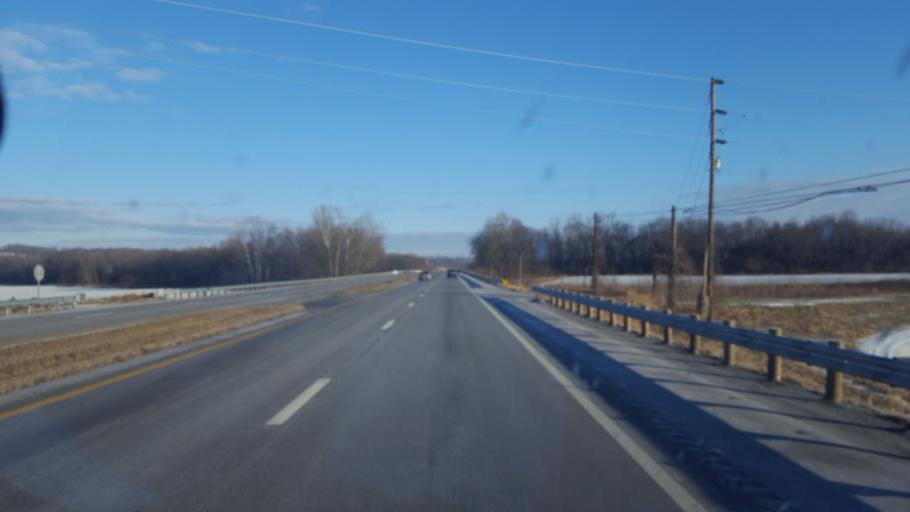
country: US
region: Ohio
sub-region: Pike County
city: Piketon
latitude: 39.0968
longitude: -83.0001
